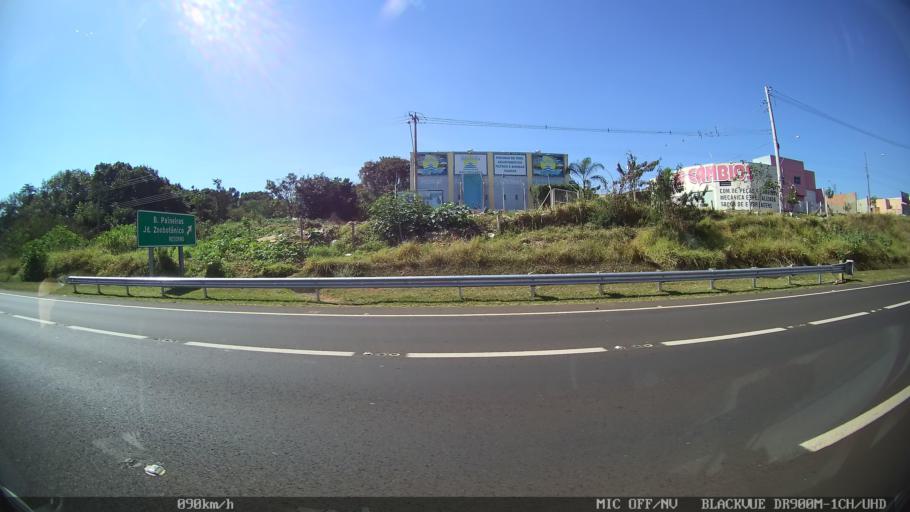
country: BR
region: Sao Paulo
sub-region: Franca
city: Franca
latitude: -20.4826
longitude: -47.4101
